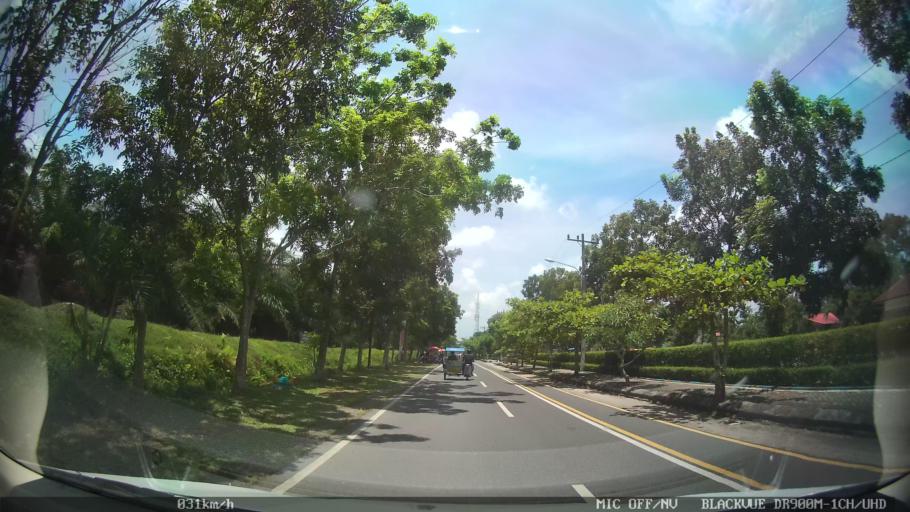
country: ID
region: North Sumatra
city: Percut
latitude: 3.5432
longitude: 98.8699
